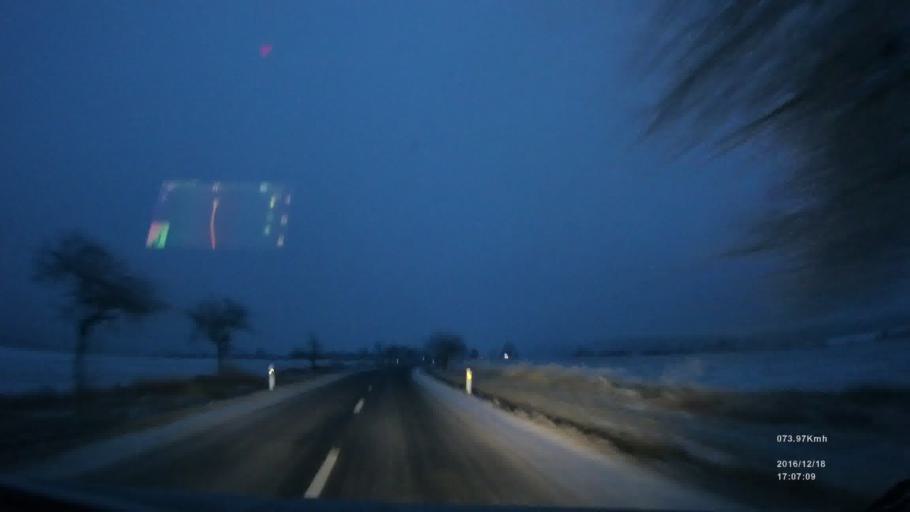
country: SK
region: Presovsky
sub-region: Okres Presov
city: Presov
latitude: 48.8996
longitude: 21.3215
